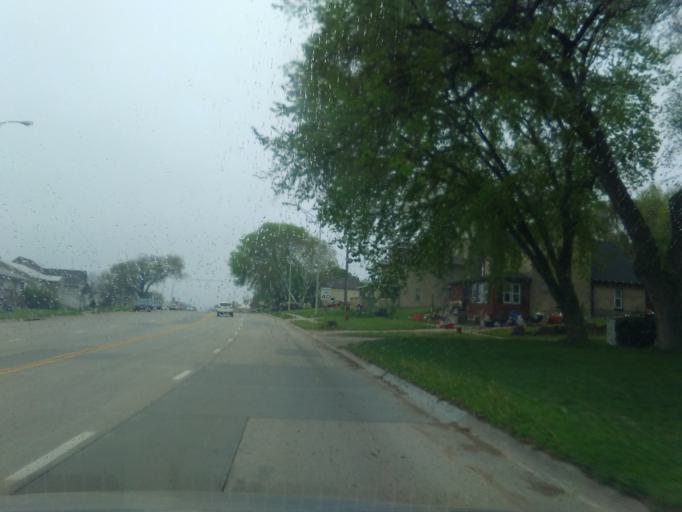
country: US
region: Nebraska
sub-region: Cuming County
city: Wisner
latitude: 41.9846
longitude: -96.9094
